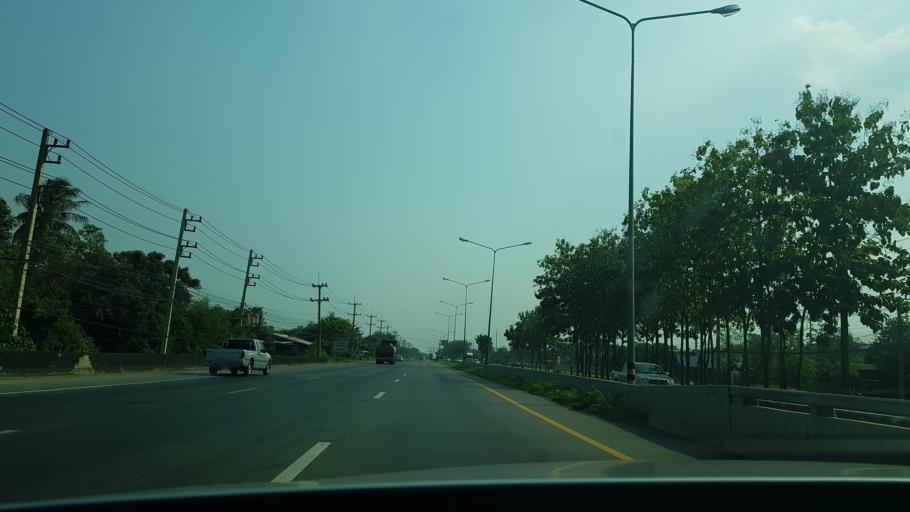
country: TH
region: Phetchaburi
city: Khao Yoi
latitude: 13.2264
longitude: 99.8250
